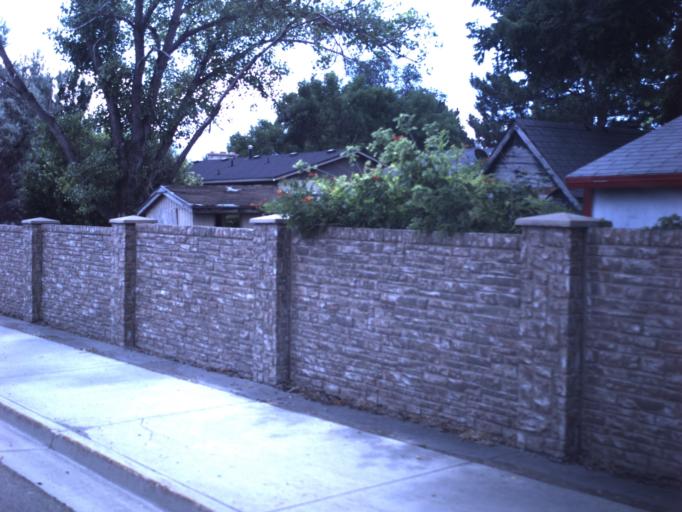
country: US
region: Utah
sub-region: Salt Lake County
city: Taylorsville
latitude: 40.6530
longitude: -111.9500
